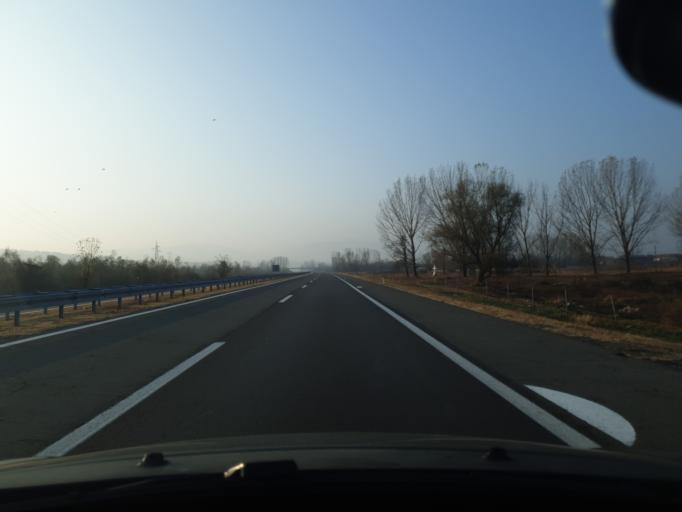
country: RS
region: Central Serbia
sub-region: Jablanicki Okrug
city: Leskovac
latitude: 42.9543
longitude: 22.0344
